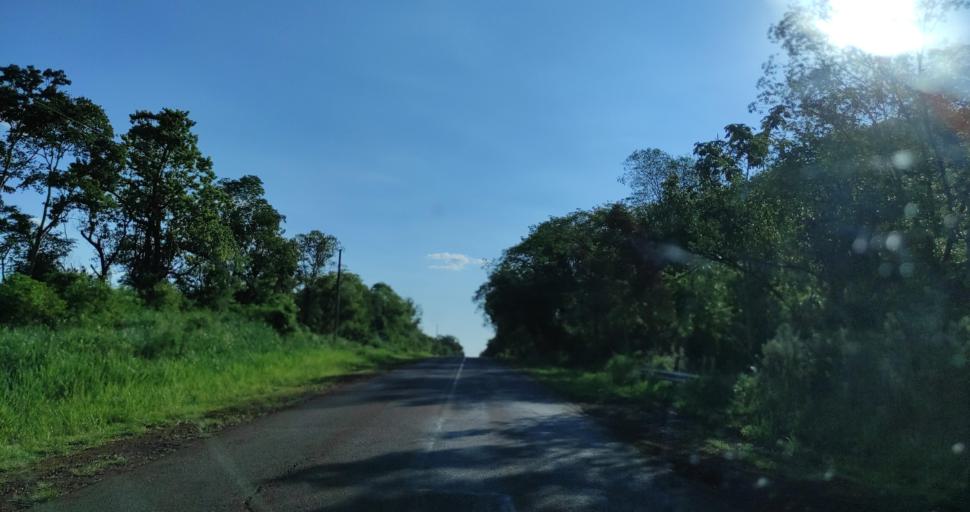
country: AR
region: Misiones
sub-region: Departamento de Eldorado
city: Eldorado
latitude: -26.3900
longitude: -54.3569
